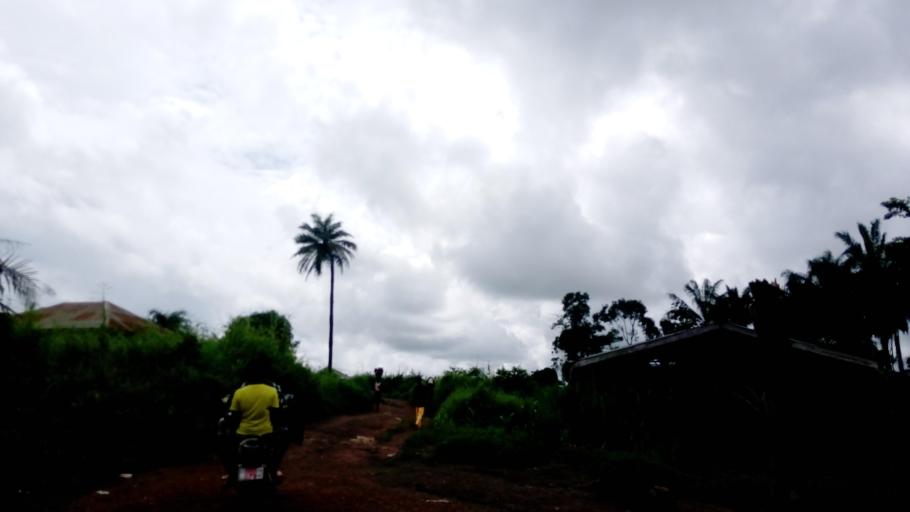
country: SL
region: Northern Province
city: Makeni
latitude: 8.8956
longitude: -12.0261
